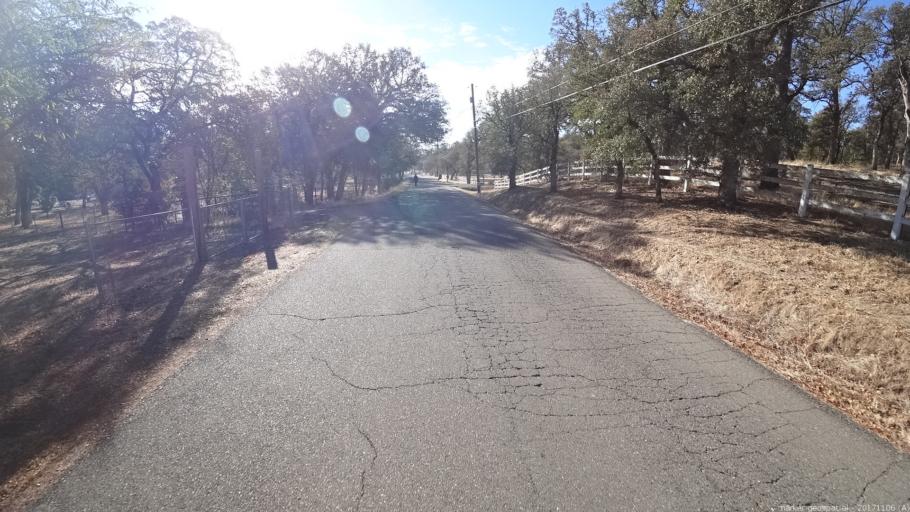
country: US
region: California
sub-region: Shasta County
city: Palo Cedro
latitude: 40.5349
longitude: -122.2475
